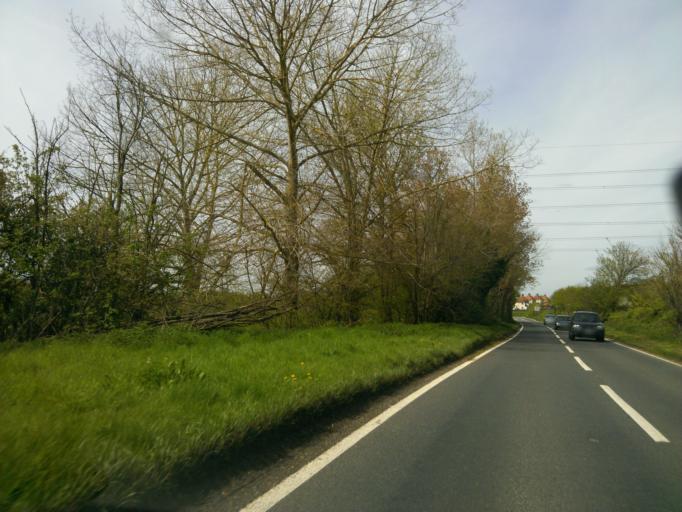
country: GB
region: England
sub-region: Essex
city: Earls Colne
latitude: 51.9266
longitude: 0.7315
